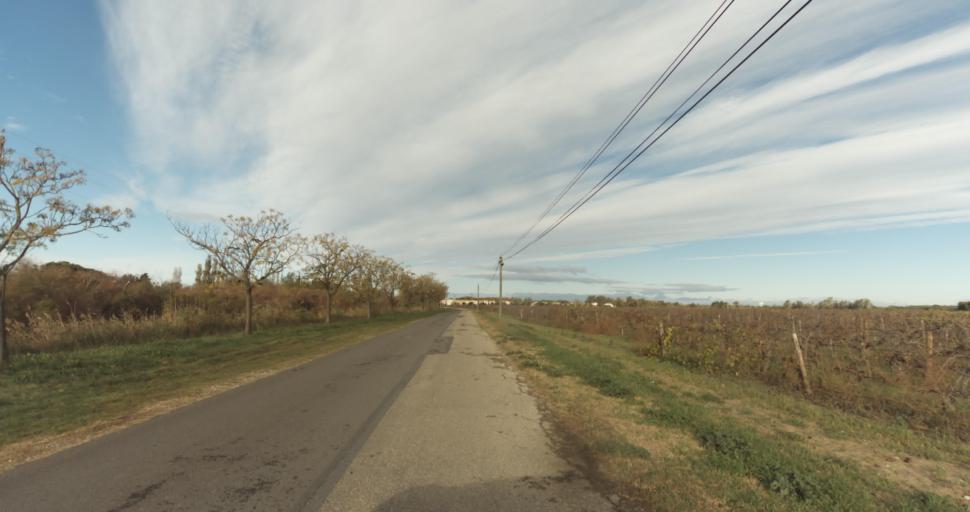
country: FR
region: Languedoc-Roussillon
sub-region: Departement du Gard
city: Aigues-Mortes
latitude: 43.5631
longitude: 4.2125
